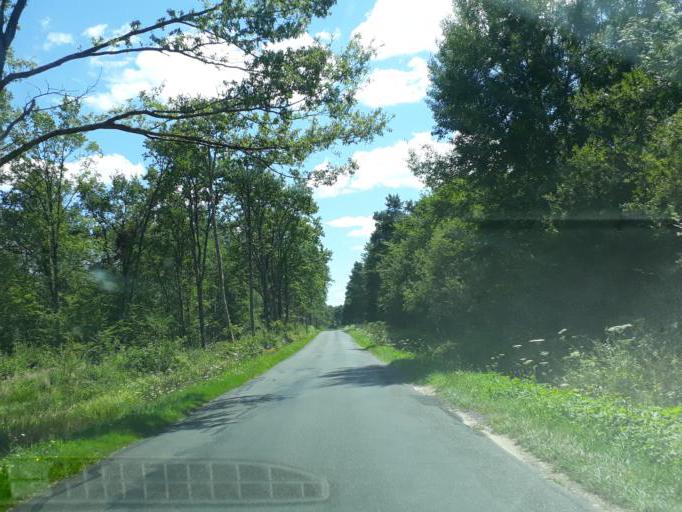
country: FR
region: Centre
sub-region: Departement du Loiret
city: Vitry-aux-Loges
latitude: 47.9355
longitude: 2.3487
